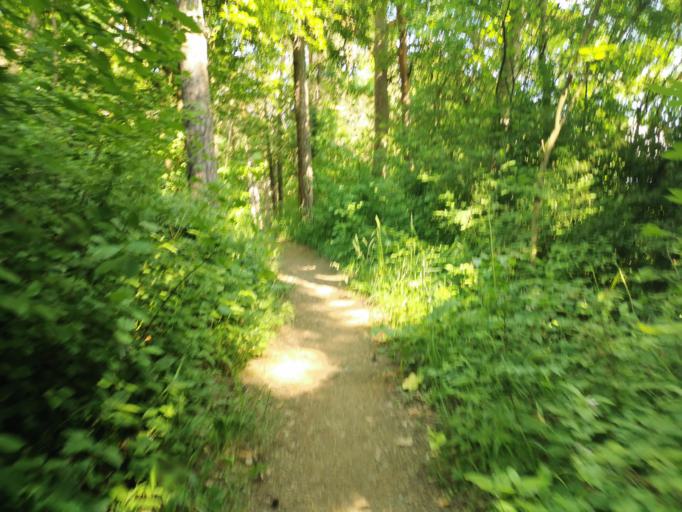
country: CZ
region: South Moravian
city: Knezdub
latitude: 48.8542
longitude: 17.3535
